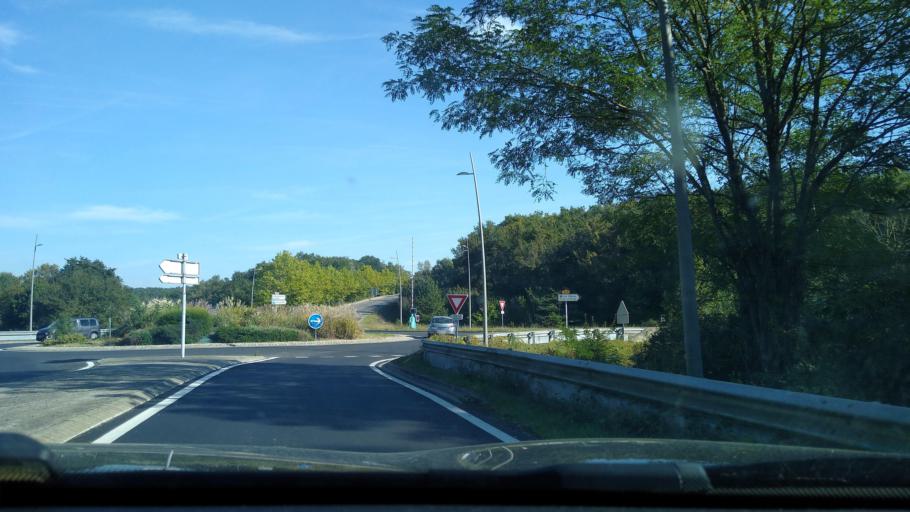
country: FR
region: Midi-Pyrenees
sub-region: Departement de la Haute-Garonne
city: Mondonville
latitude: 43.6718
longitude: 1.2930
